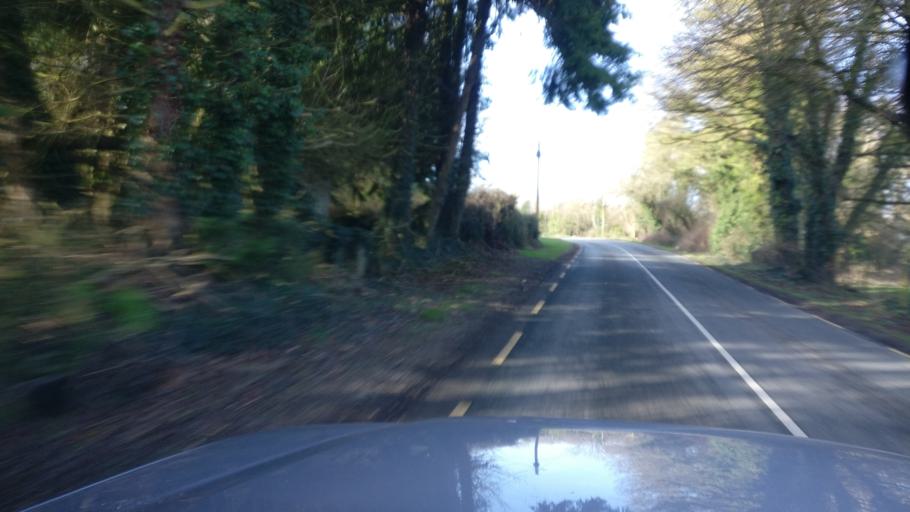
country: IE
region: Leinster
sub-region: Laois
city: Stradbally
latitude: 52.9673
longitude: -7.2070
